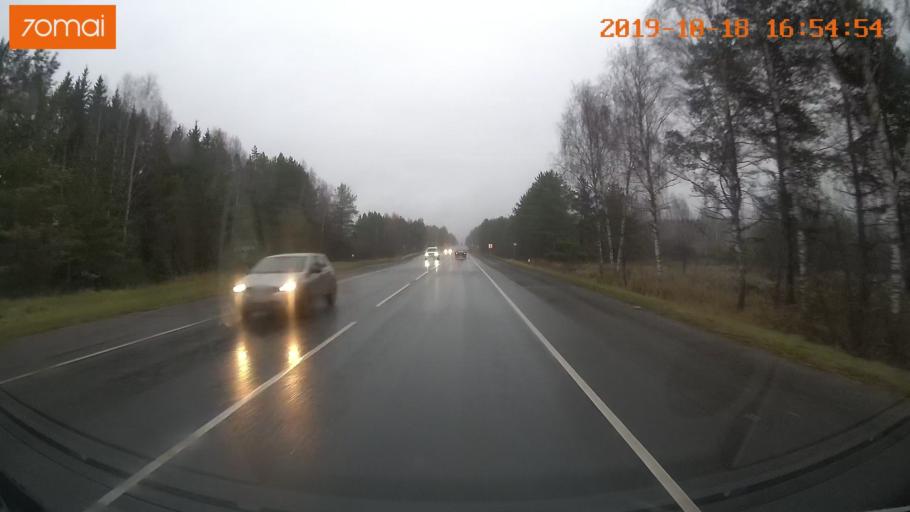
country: RU
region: Ivanovo
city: Novoye Leushino
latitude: 56.6363
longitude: 40.5744
